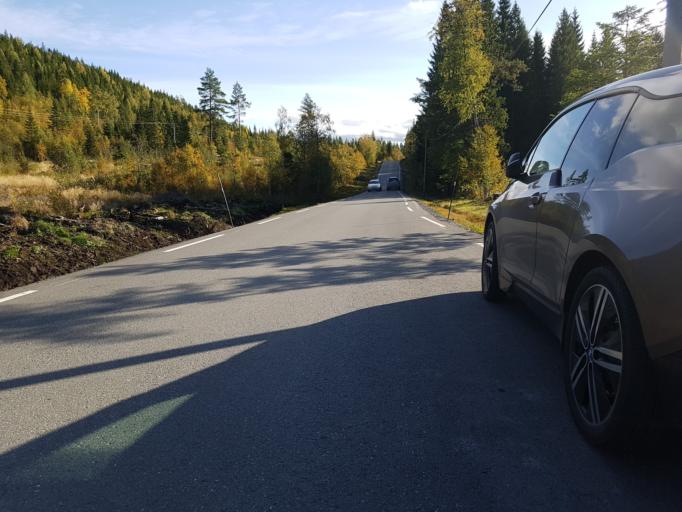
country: NO
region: Sor-Trondelag
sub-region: Malvik
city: Malvik
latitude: 63.3719
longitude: 10.6139
